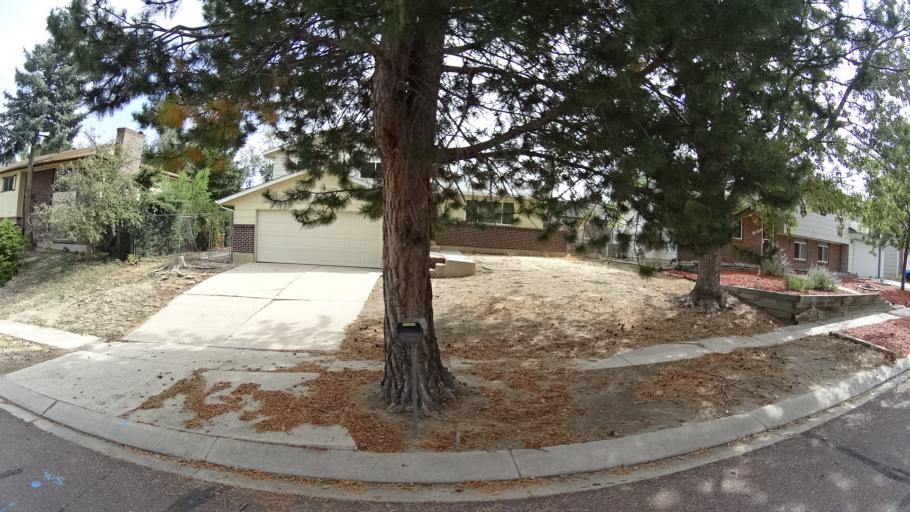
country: US
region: Colorado
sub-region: El Paso County
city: Cimarron Hills
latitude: 38.8597
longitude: -104.7299
